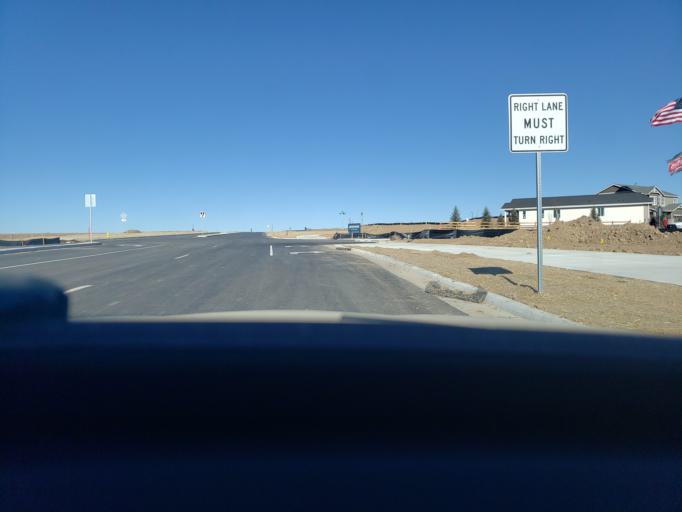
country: US
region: Colorado
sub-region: Adams County
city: Aurora
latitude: 39.7724
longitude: -104.7064
